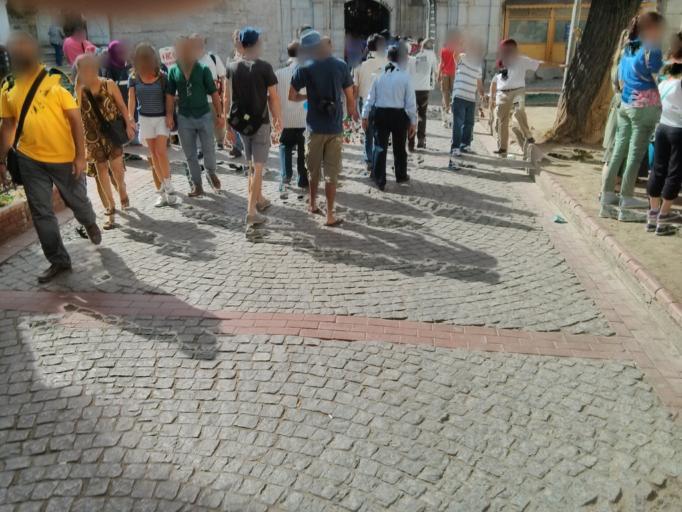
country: TR
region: Istanbul
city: Arikoey
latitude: 41.2461
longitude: 29.0369
